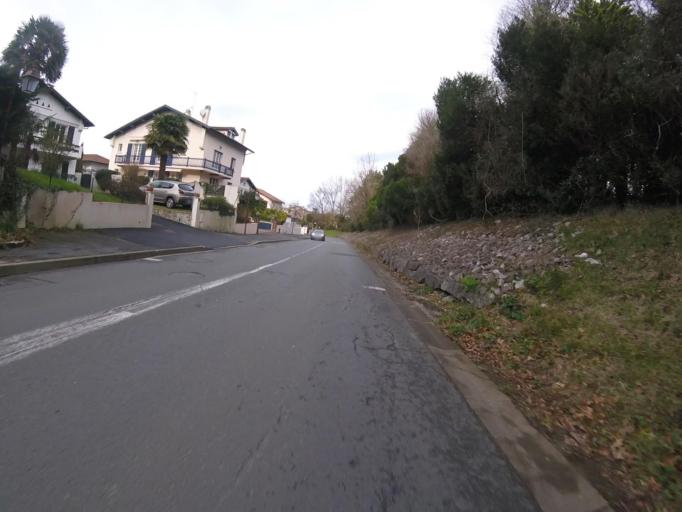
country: FR
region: Aquitaine
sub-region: Departement des Pyrenees-Atlantiques
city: Saint-Jean-de-Luz
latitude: 43.3778
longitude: -1.6589
